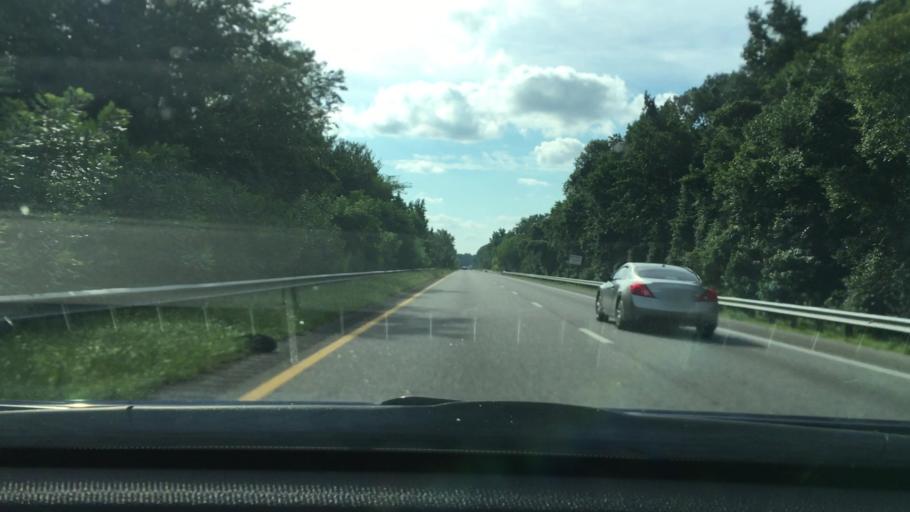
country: US
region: South Carolina
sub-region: Dorchester County
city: Ridgeville
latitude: 33.1457
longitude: -80.3277
